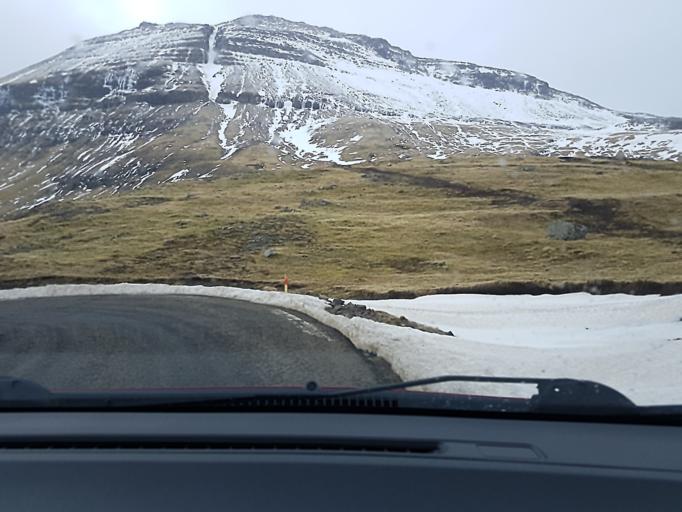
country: FO
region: Streymoy
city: Kollafjordhur
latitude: 62.0547
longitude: -6.9193
